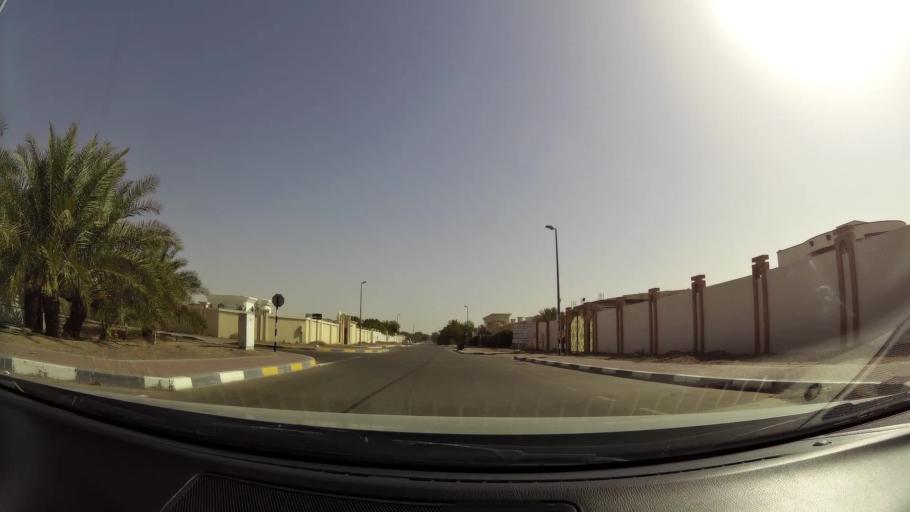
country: OM
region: Al Buraimi
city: Al Buraymi
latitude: 24.3362
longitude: 55.7927
